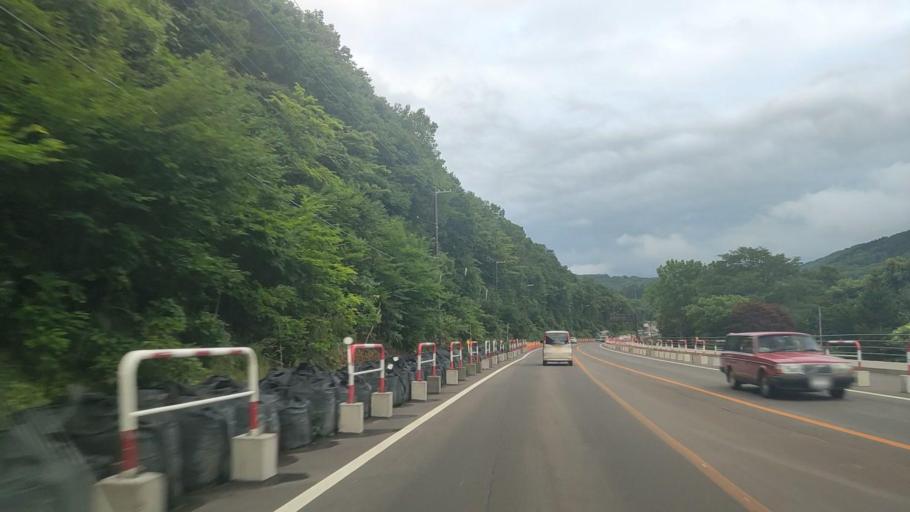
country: JP
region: Hokkaido
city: Nanae
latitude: 41.9872
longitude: 140.6395
